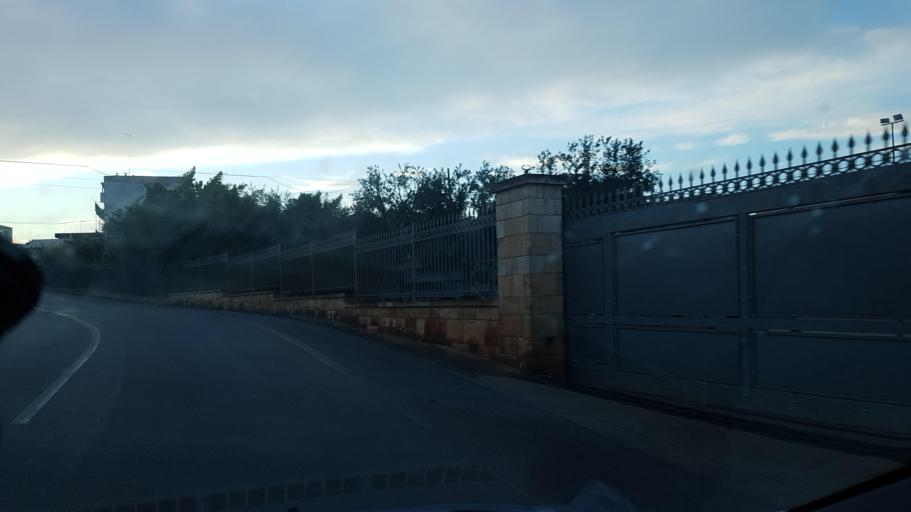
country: IT
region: Apulia
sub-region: Provincia di Brindisi
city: Ceglie Messapica
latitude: 40.6458
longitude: 17.5252
